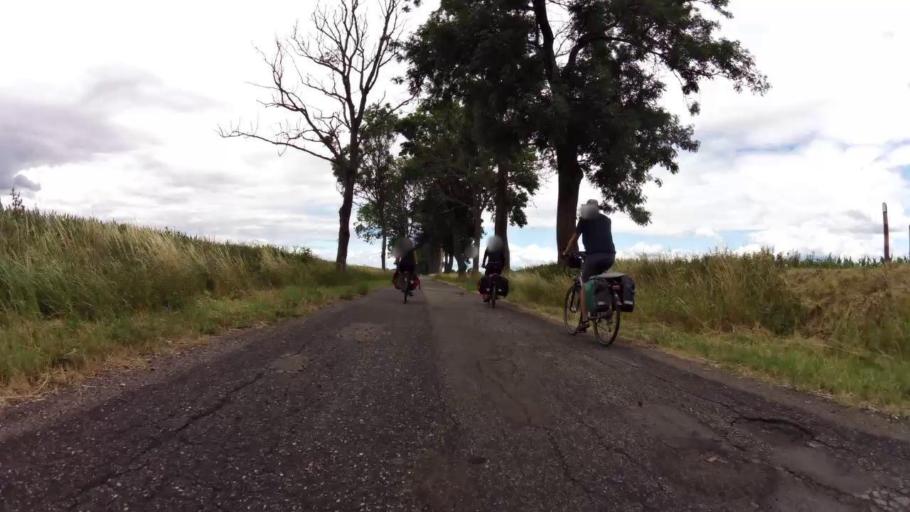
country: PL
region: West Pomeranian Voivodeship
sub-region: Powiat lobeski
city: Lobez
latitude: 53.7587
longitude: 15.5750
